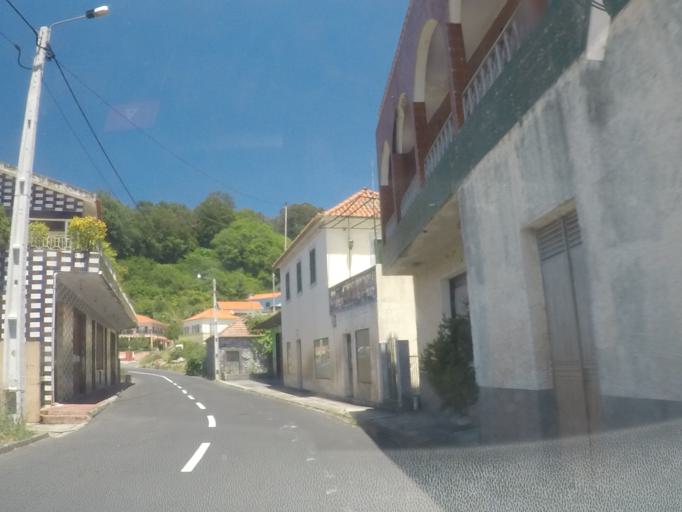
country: PT
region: Madeira
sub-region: Camara de Lobos
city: Curral das Freiras
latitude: 32.6878
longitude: -16.9932
